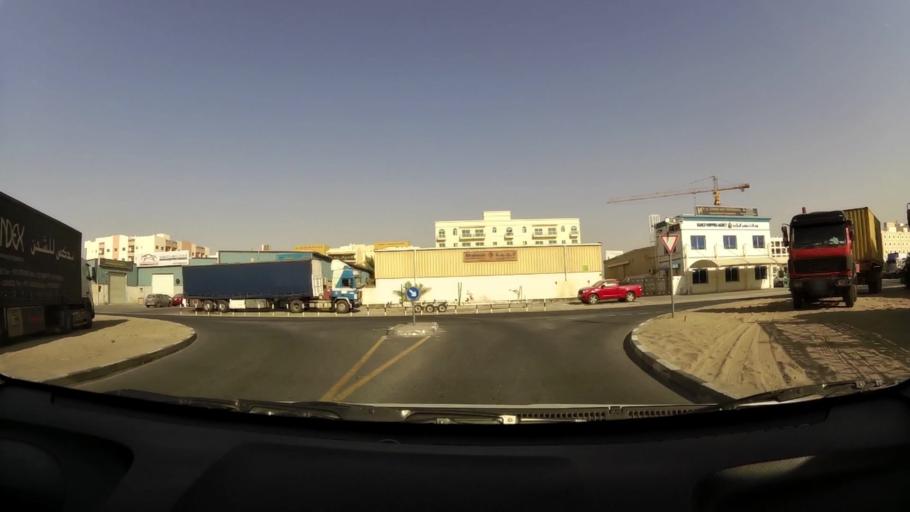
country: AE
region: Ash Shariqah
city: Sharjah
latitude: 25.2821
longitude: 55.3852
